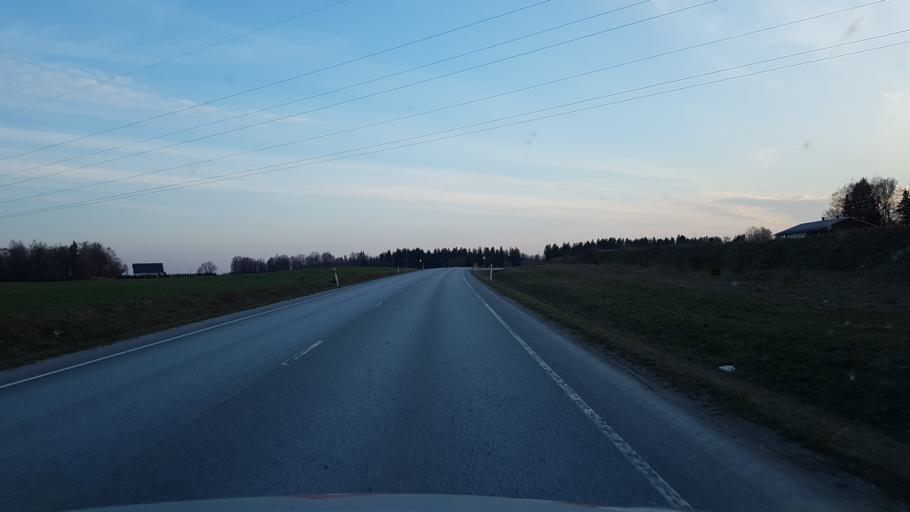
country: EE
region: Laeaene-Virumaa
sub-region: Rakvere linn
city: Rakvere
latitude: 59.3290
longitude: 26.3989
